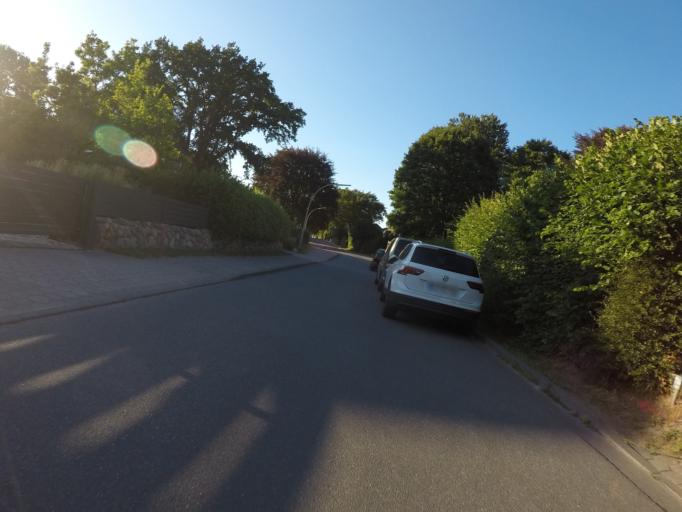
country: DE
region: Hamburg
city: Duvenstedt
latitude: 53.7011
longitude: 10.1115
